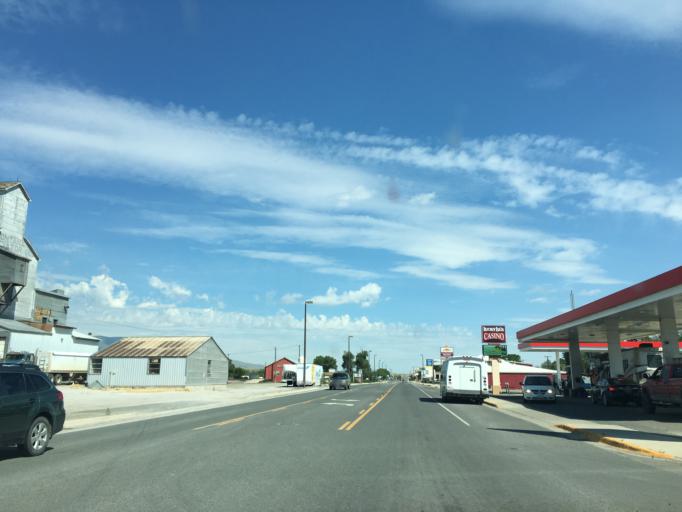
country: US
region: Montana
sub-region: Broadwater County
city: Townsend
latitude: 46.3203
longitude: -111.5221
